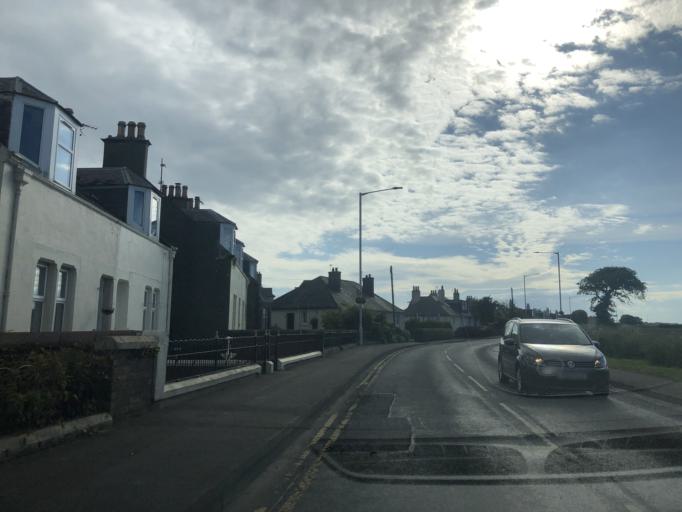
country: GB
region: Scotland
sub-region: Fife
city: Saint Monance
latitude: 56.2079
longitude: -2.7624
